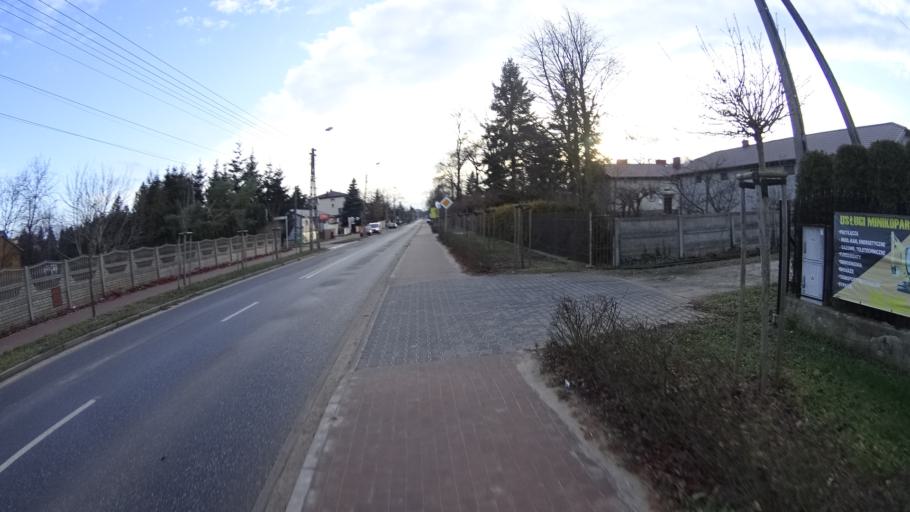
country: PL
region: Masovian Voivodeship
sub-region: Powiat warszawski zachodni
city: Ozarow Mazowiecki
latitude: 52.2196
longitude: 20.8005
